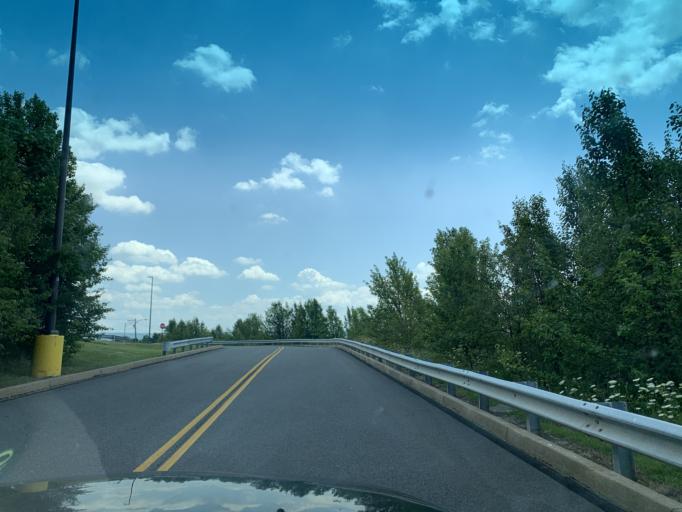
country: US
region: Pennsylvania
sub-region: Lackawanna County
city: Chinchilla
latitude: 41.4621
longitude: -75.6526
